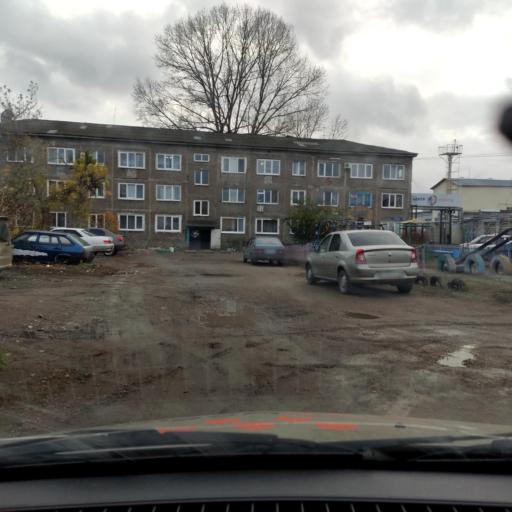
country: RU
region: Bashkortostan
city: Ufa
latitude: 54.7848
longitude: 56.0678
